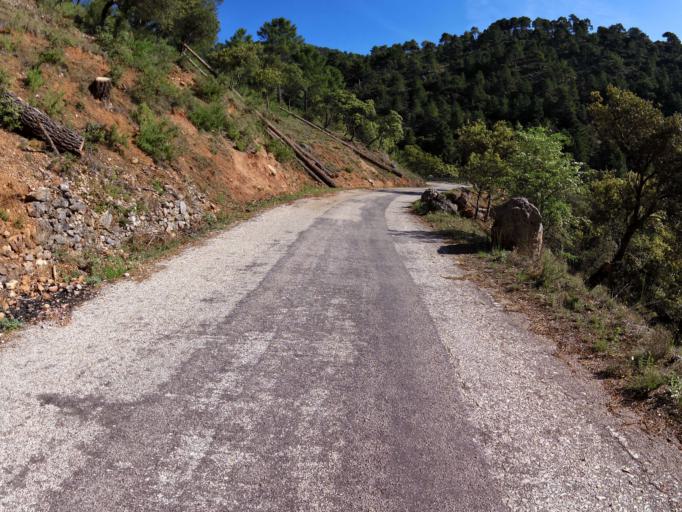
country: ES
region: Castille-La Mancha
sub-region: Provincia de Albacete
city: Riopar
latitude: 38.5226
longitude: -2.4558
